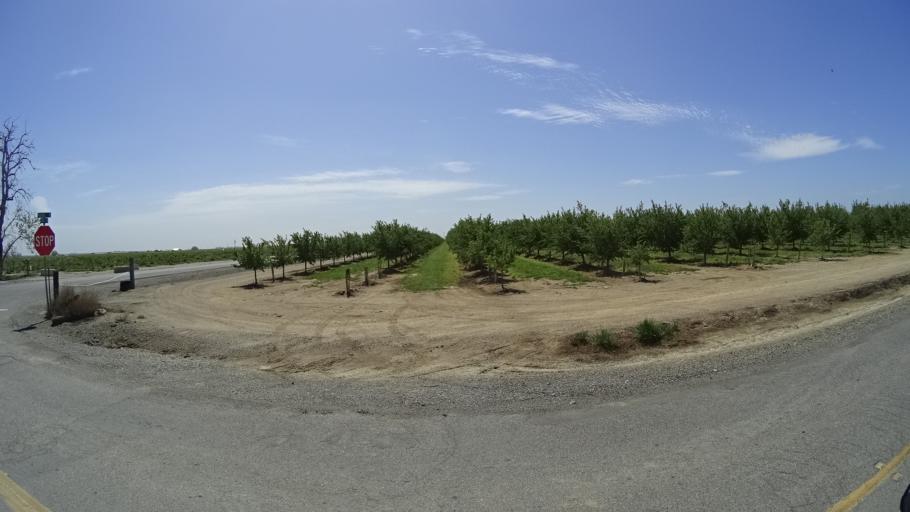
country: US
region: California
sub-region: Glenn County
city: Orland
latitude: 39.6527
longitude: -122.1410
